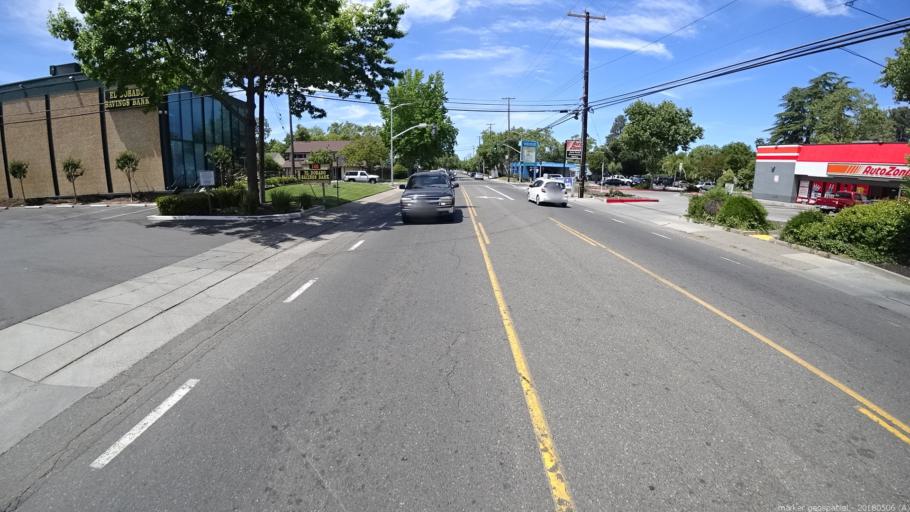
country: US
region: California
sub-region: Sacramento County
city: Sacramento
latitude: 38.5587
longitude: -121.4387
